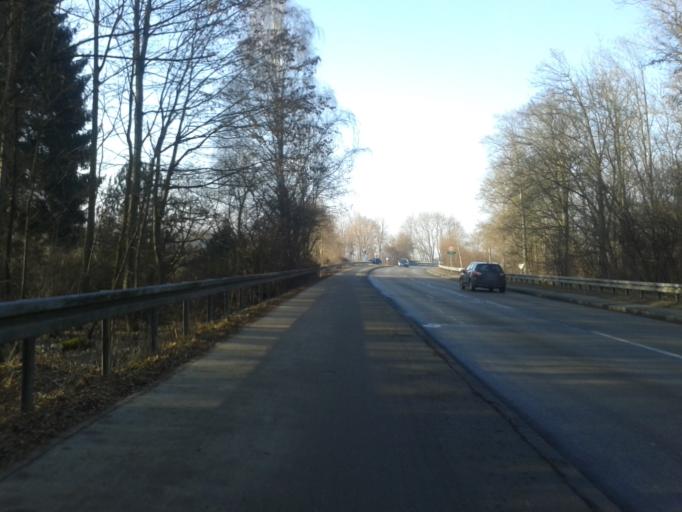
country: DE
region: Baden-Wuerttemberg
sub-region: Tuebingen Region
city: Ulm
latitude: 48.3690
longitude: 9.9897
